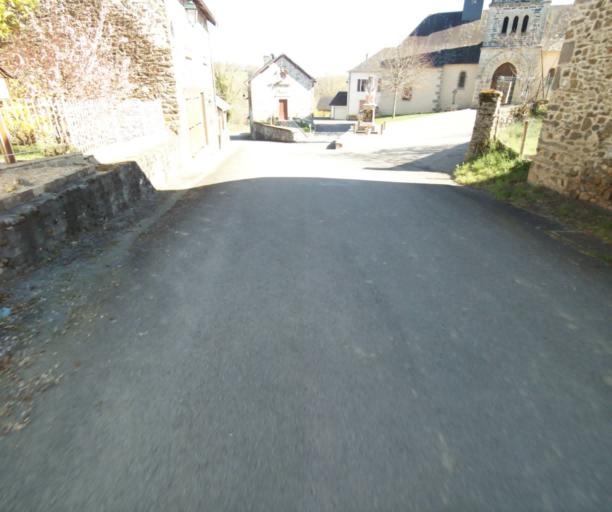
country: FR
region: Limousin
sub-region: Departement de la Correze
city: Chamboulive
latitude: 45.4230
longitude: 1.6485
